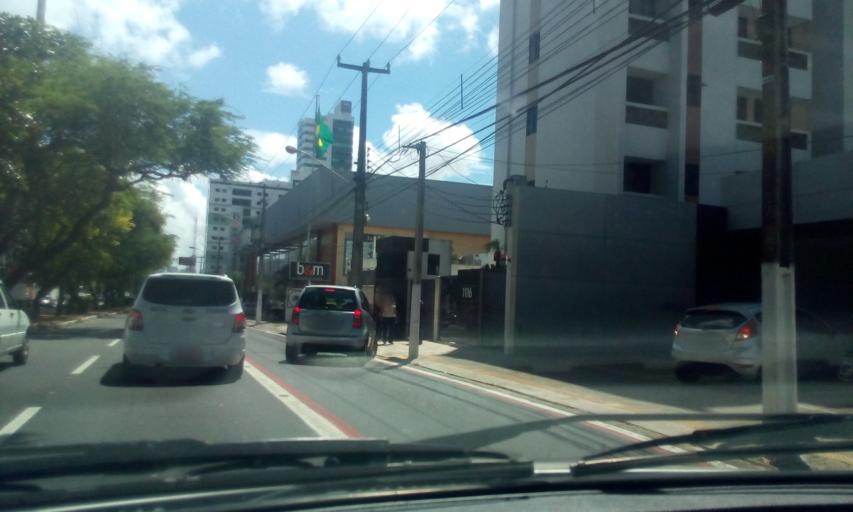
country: BR
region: Rio Grande do Norte
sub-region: Natal
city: Natal
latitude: -5.7921
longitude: -35.2029
